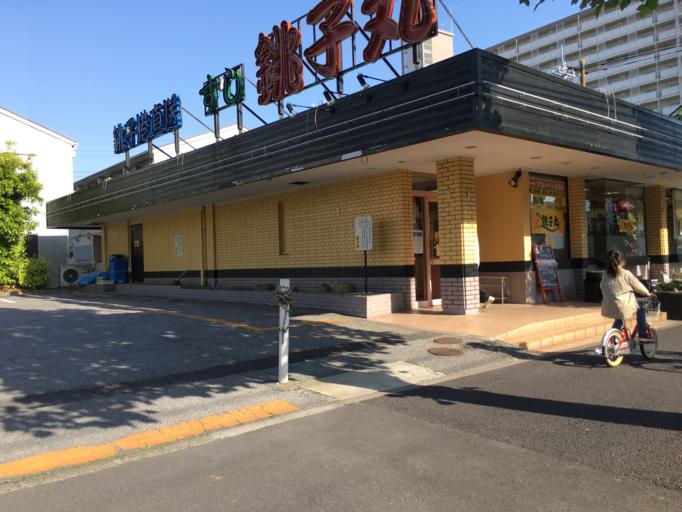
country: JP
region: Chiba
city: Nagareyama
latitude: 35.8232
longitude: 139.9146
